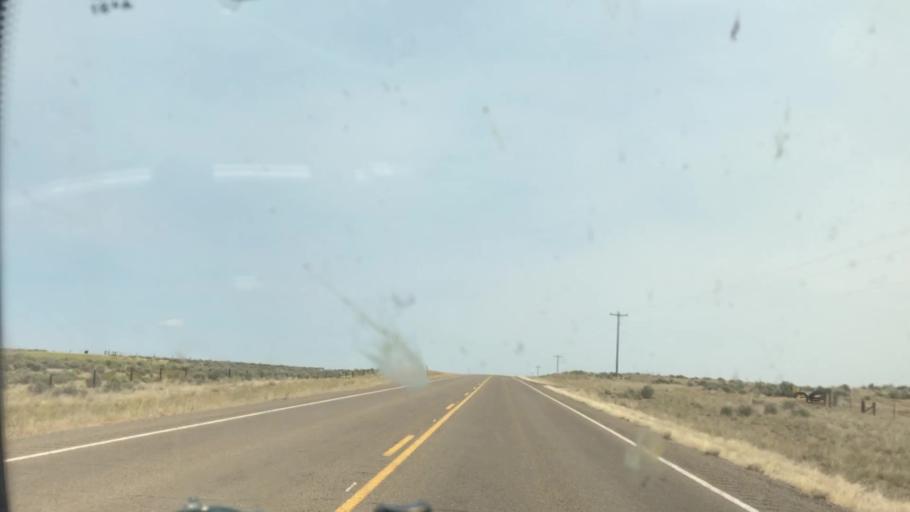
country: US
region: Idaho
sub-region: Owyhee County
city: Homedale
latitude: 42.8571
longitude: -117.5715
